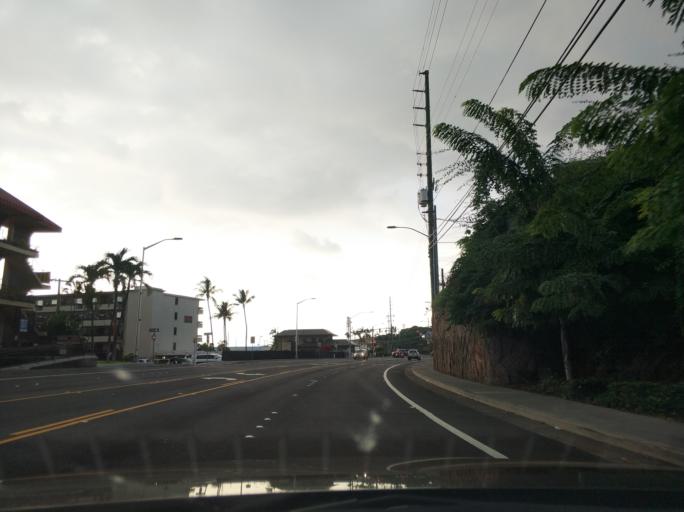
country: US
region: Hawaii
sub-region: Hawaii County
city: Kailua-Kona
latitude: 19.6412
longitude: -155.9951
